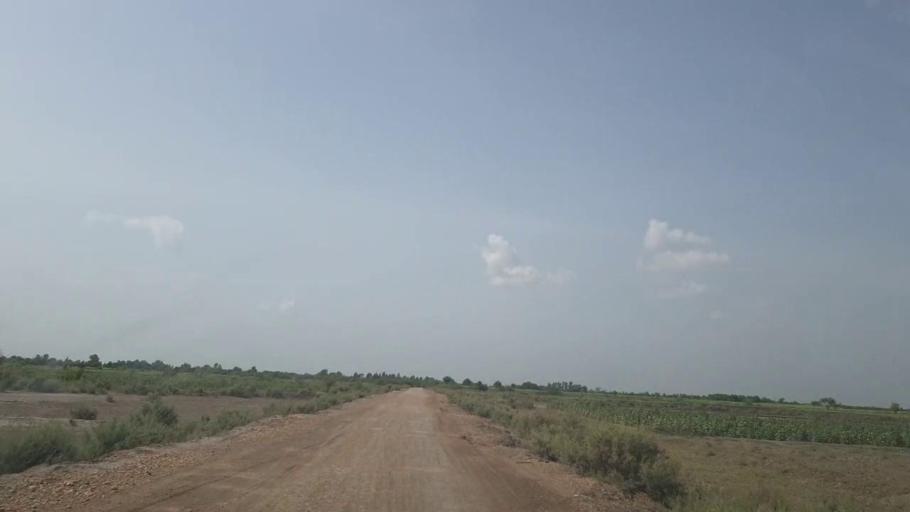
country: PK
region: Sindh
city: Tando Bago
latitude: 24.7746
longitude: 69.1306
